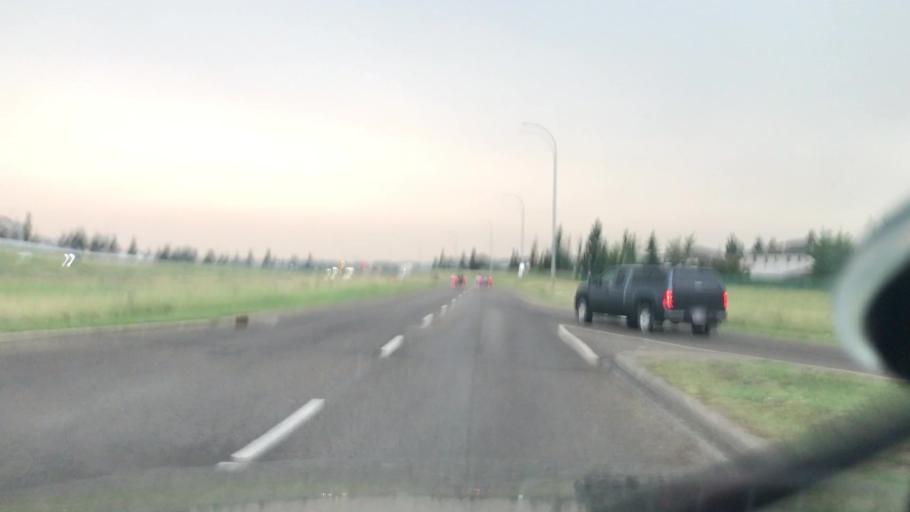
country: CA
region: Alberta
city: Edmonton
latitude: 53.4576
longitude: -113.5900
